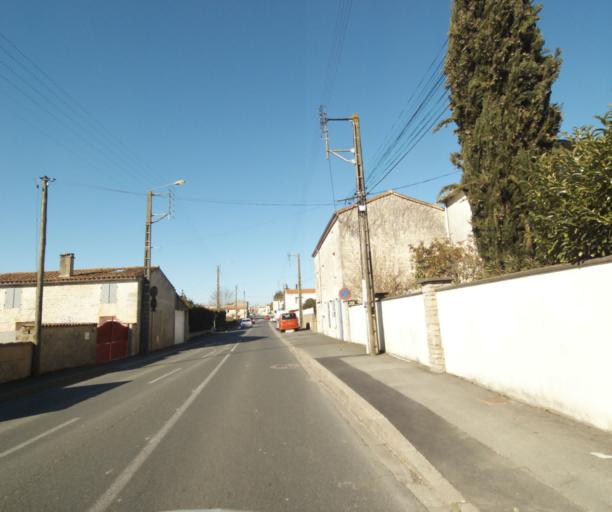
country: FR
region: Poitou-Charentes
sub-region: Departement des Deux-Sevres
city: Niort
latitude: 46.3487
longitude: -0.4775
